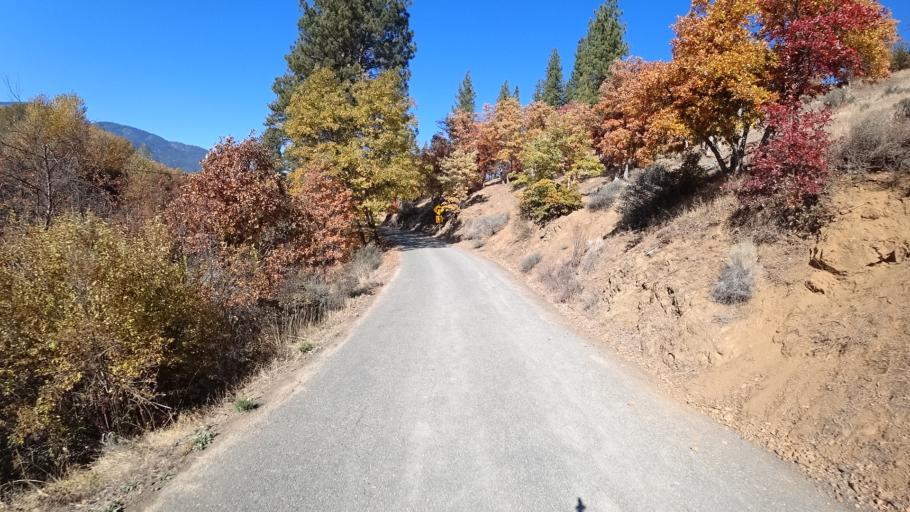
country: US
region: California
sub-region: Siskiyou County
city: Yreka
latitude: 41.6063
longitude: -122.9613
